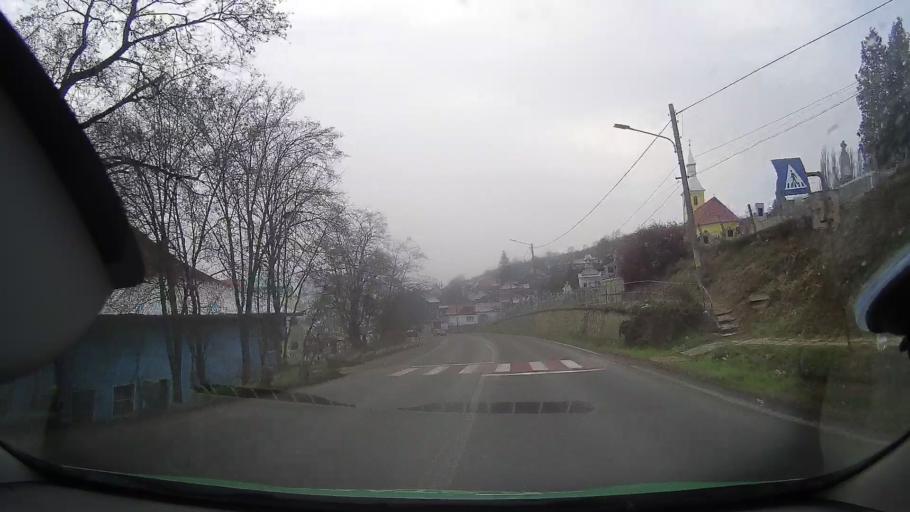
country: RO
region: Mures
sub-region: Municipiul Tarnaveni
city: Tarnaveni
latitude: 46.3348
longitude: 24.2873
